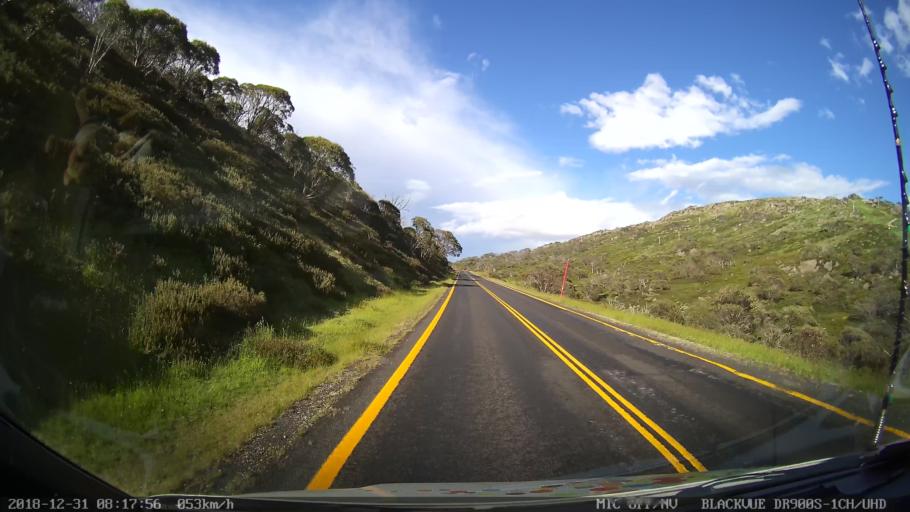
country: AU
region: New South Wales
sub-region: Snowy River
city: Jindabyne
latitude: -36.4119
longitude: 148.4000
